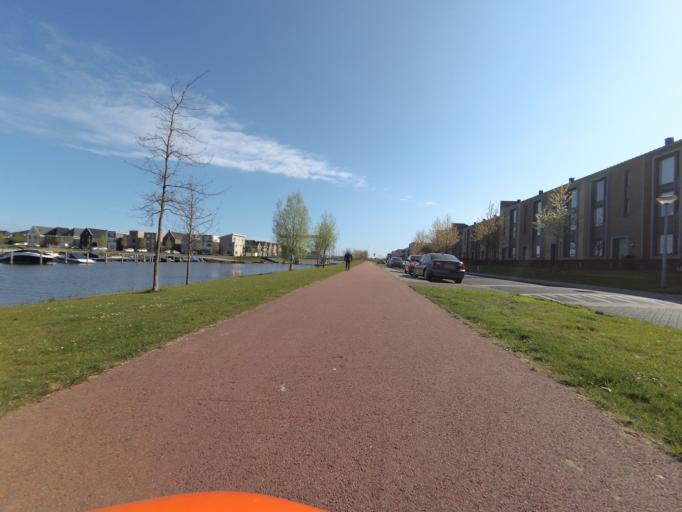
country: NL
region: Flevoland
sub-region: Gemeente Almere
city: Almere Stad
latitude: 52.3970
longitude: 5.1717
